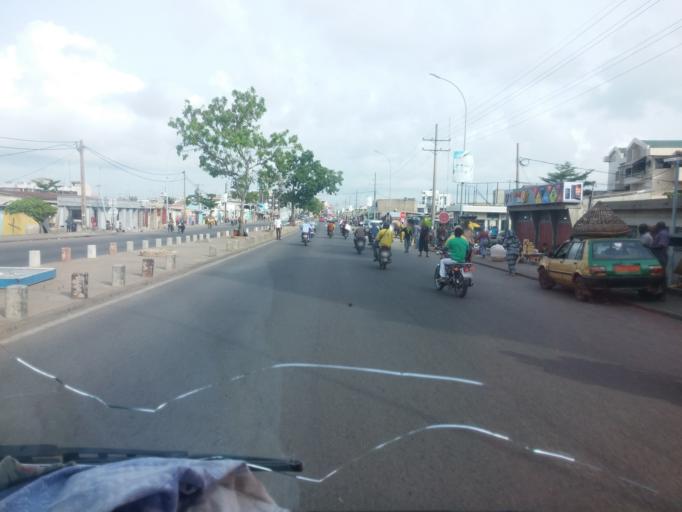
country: BJ
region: Littoral
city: Cotonou
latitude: 6.3723
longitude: 2.4089
